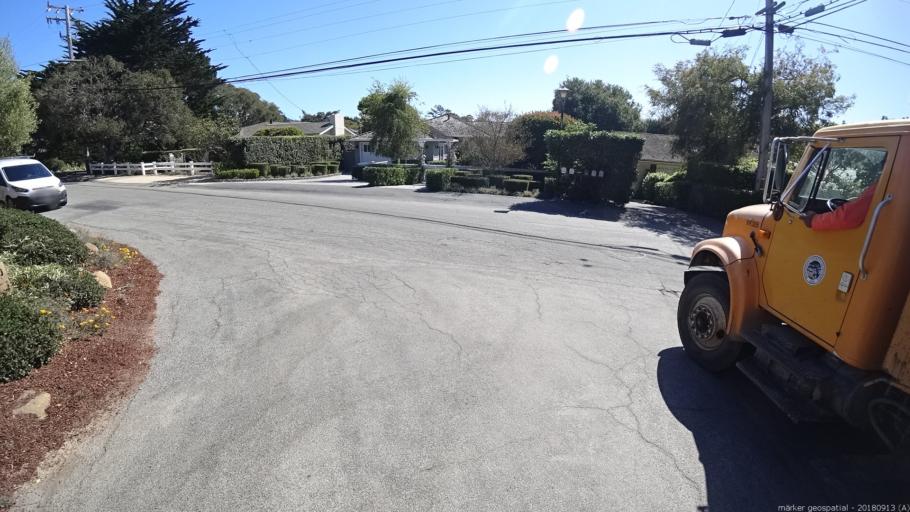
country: US
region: California
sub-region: Monterey County
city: Carmel-by-the-Sea
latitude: 36.5419
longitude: -121.9283
